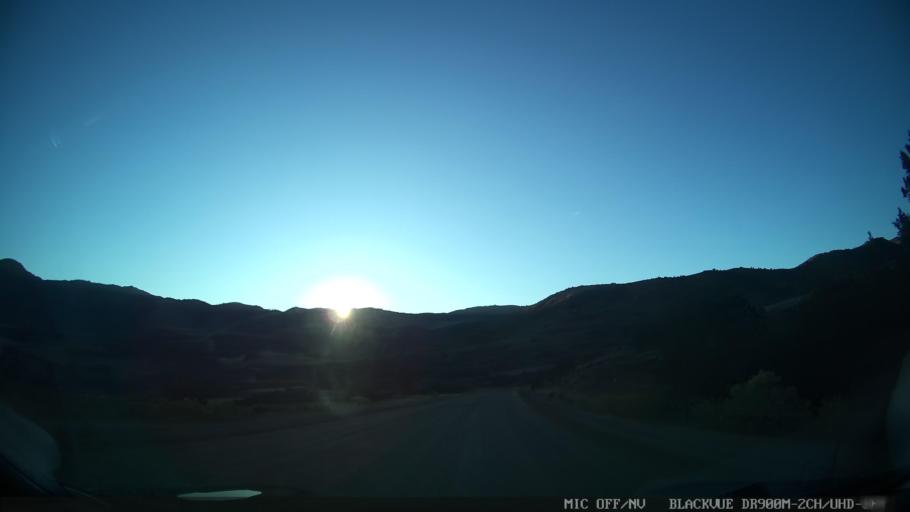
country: US
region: Colorado
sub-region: Grand County
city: Kremmling
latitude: 39.9666
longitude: -106.5166
